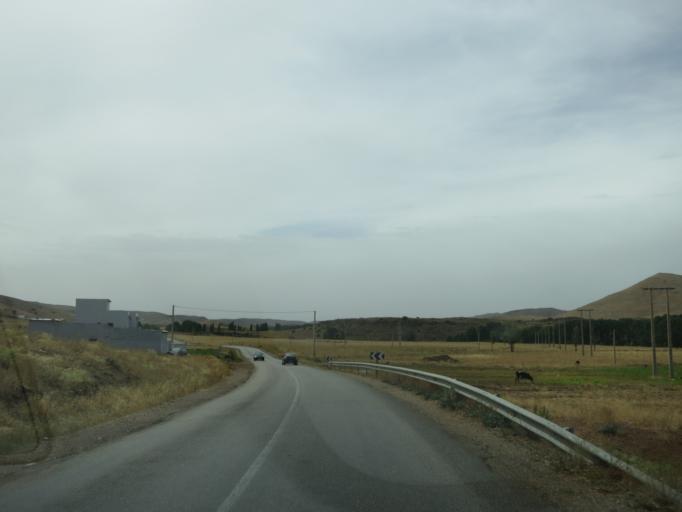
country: MA
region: Meknes-Tafilalet
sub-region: Ifrane
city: Azrou
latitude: 33.2007
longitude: -5.0638
